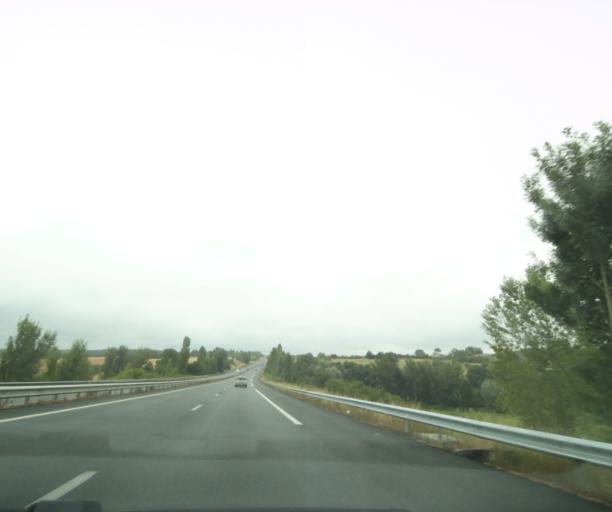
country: FR
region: Midi-Pyrenees
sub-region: Departement de la Haute-Garonne
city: Montastruc-la-Conseillere
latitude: 43.7356
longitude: 1.5825
